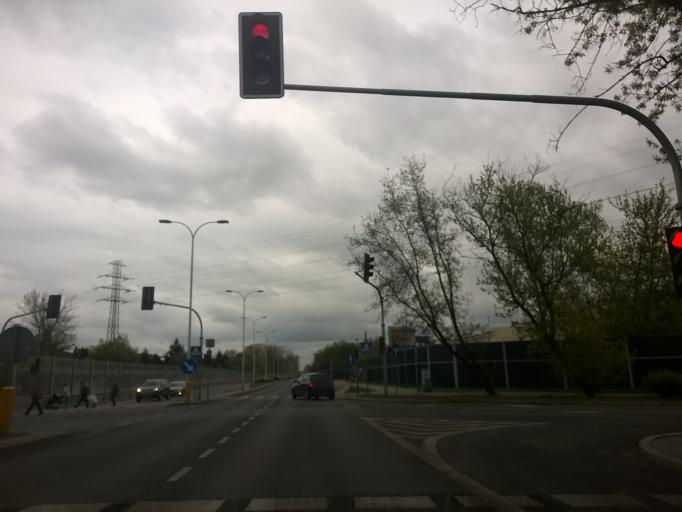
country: PL
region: Masovian Voivodeship
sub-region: Warszawa
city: Ursynow
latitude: 52.1725
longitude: 21.0553
